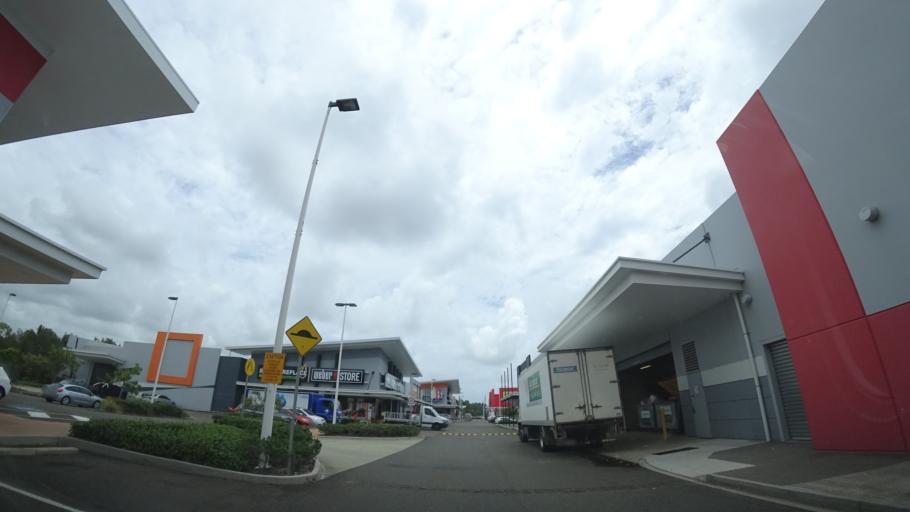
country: AU
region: Queensland
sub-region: Sunshine Coast
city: Dicky Beach
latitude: -26.7355
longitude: 153.1198
